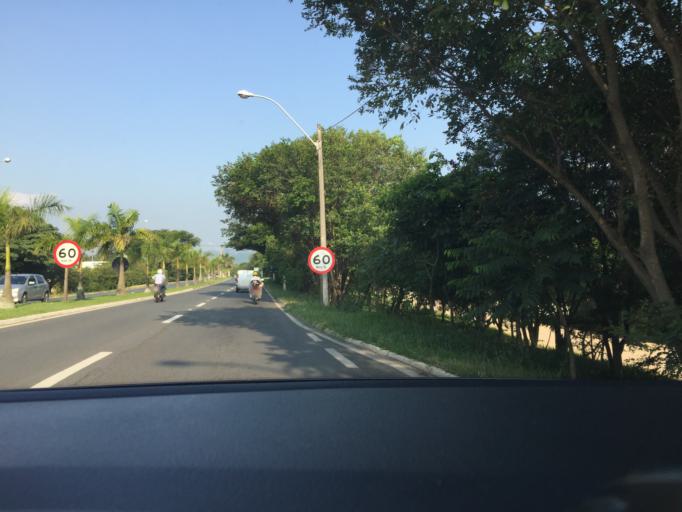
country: BR
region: Sao Paulo
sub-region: Valinhos
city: Valinhos
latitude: -23.0080
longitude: -47.0187
